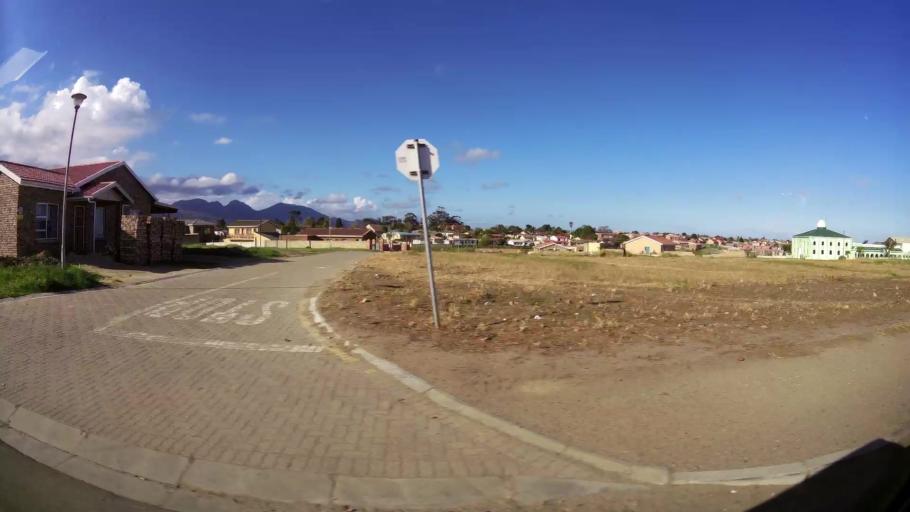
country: ZA
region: Western Cape
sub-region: Eden District Municipality
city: George
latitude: -33.9706
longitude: 22.4826
